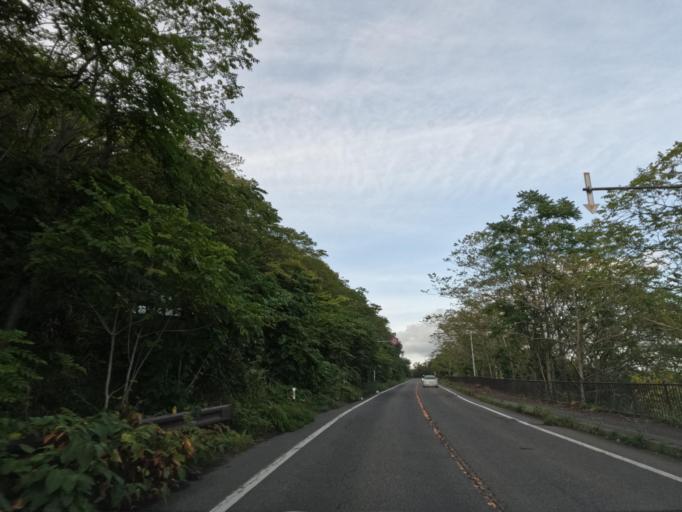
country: JP
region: Hokkaido
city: Date
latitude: 42.5226
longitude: 140.8610
